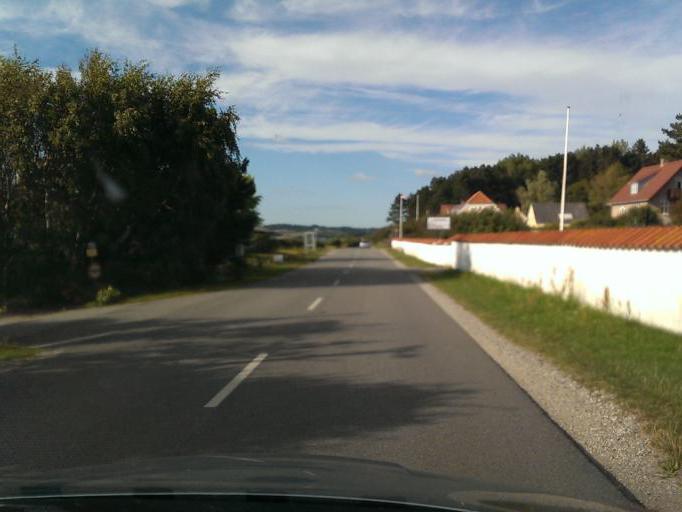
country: DK
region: Central Jutland
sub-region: Syddjurs Kommune
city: Ronde
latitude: 56.1471
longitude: 10.5202
